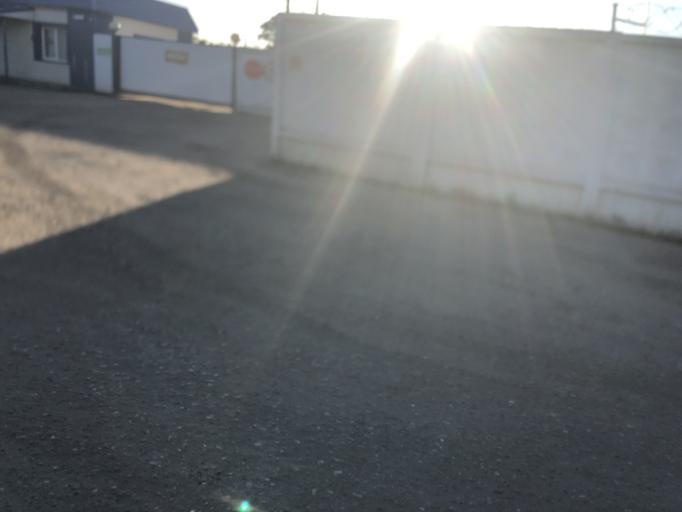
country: RU
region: Tverskaya
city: Rzhev
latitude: 56.2462
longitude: 34.3011
